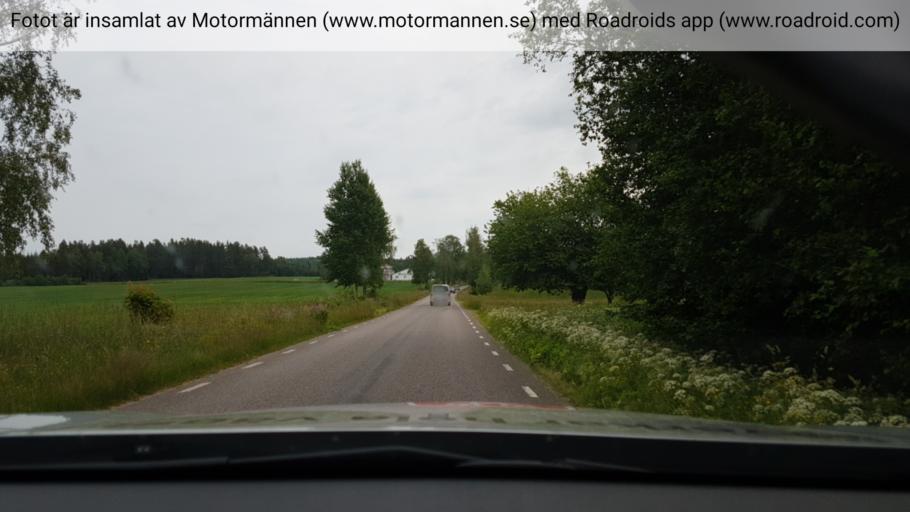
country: SE
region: Vaestra Goetaland
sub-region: Tidaholms Kommun
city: Tidaholm
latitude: 58.0701
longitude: 13.9387
